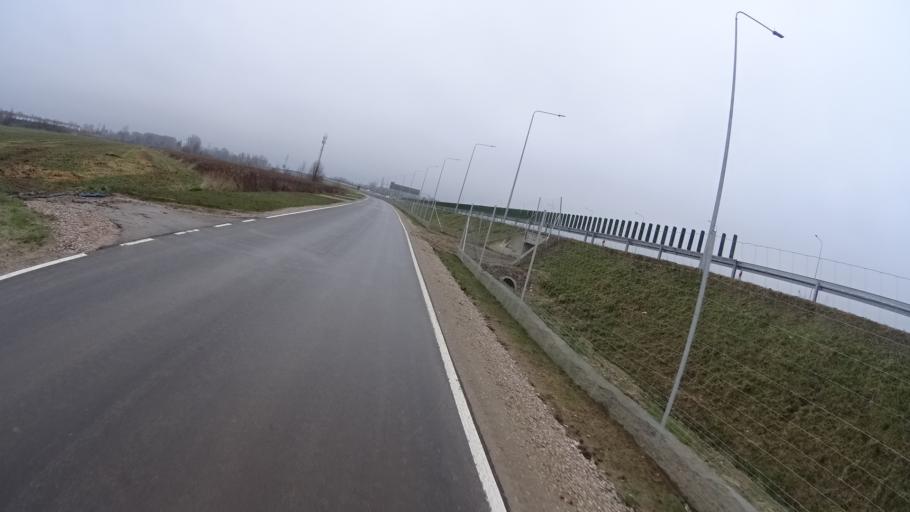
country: PL
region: Masovian Voivodeship
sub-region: Warszawa
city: Wilanow
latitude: 52.1514
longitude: 21.1021
